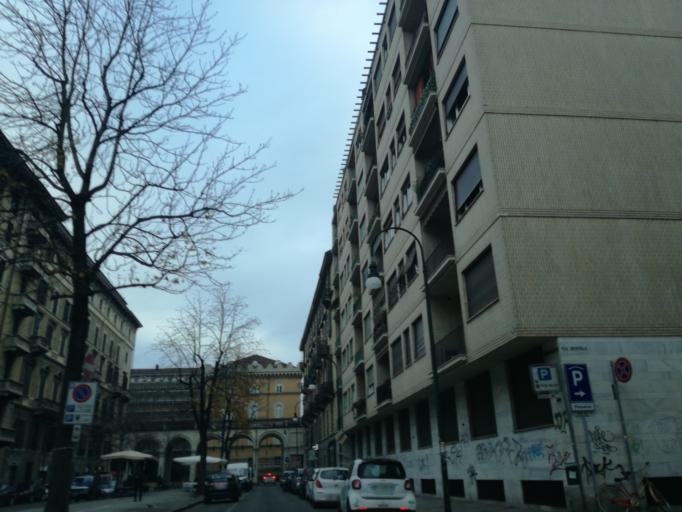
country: IT
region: Piedmont
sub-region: Provincia di Torino
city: Turin
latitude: 45.0734
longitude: 7.6720
